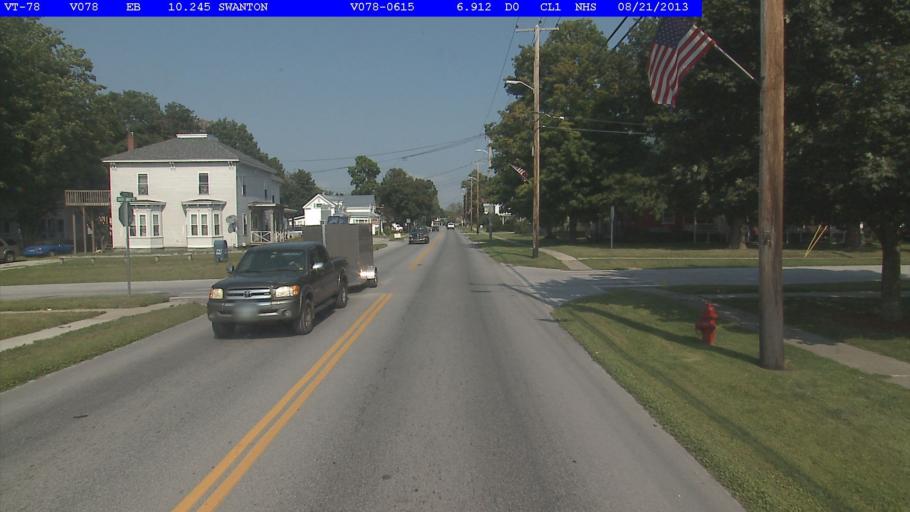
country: US
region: Vermont
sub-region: Franklin County
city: Swanton
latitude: 44.9190
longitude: -73.1219
